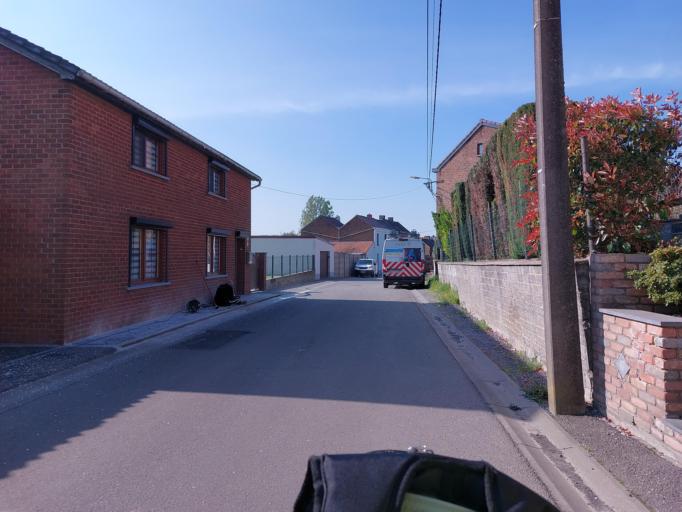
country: BE
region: Wallonia
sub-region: Province du Hainaut
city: Ecaussinnes-d'Enghien
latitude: 50.5566
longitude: 4.1603
